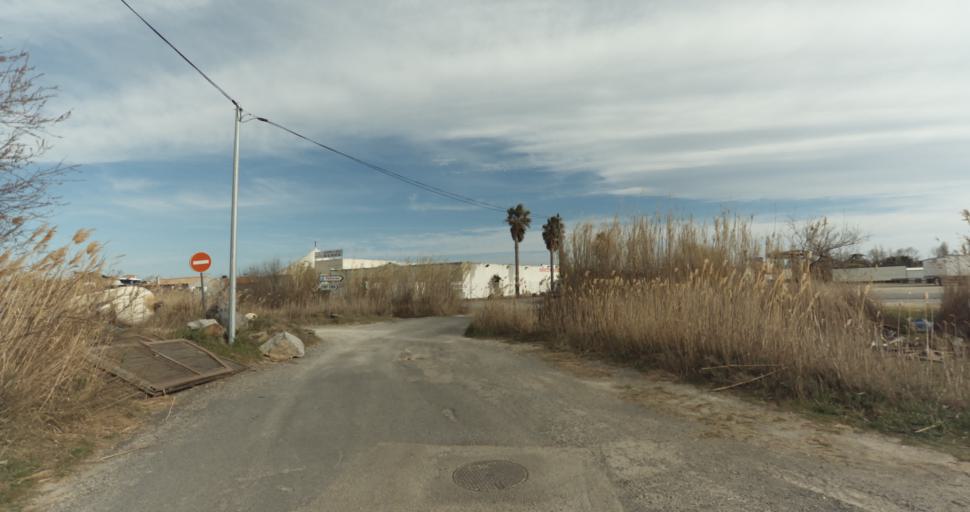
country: FR
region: Languedoc-Roussillon
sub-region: Departement de l'Herault
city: Marseillan
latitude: 43.3221
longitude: 3.5478
